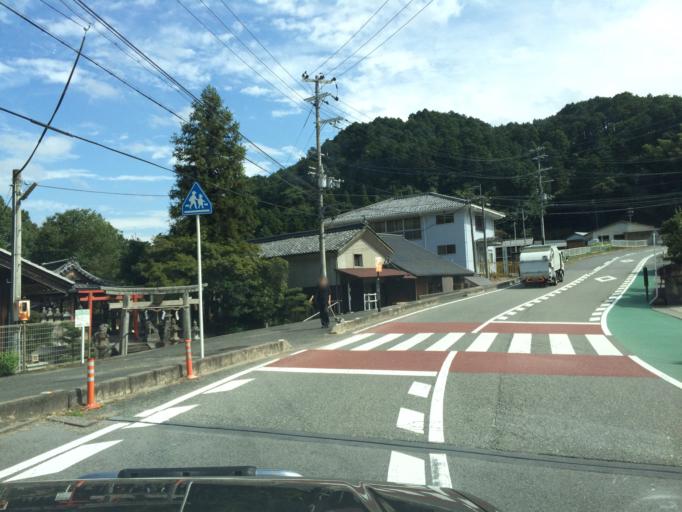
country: JP
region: Mie
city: Nabari
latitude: 34.6804
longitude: 136.0301
